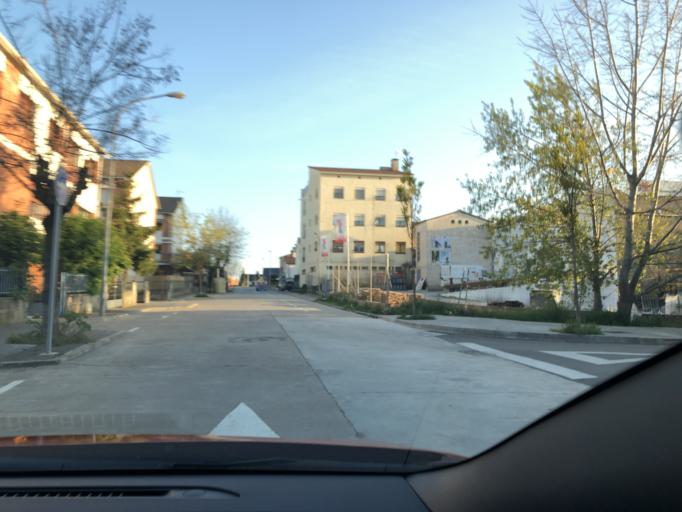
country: ES
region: Catalonia
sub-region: Provincia de Lleida
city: Solsona
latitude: 41.9908
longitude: 1.5150
